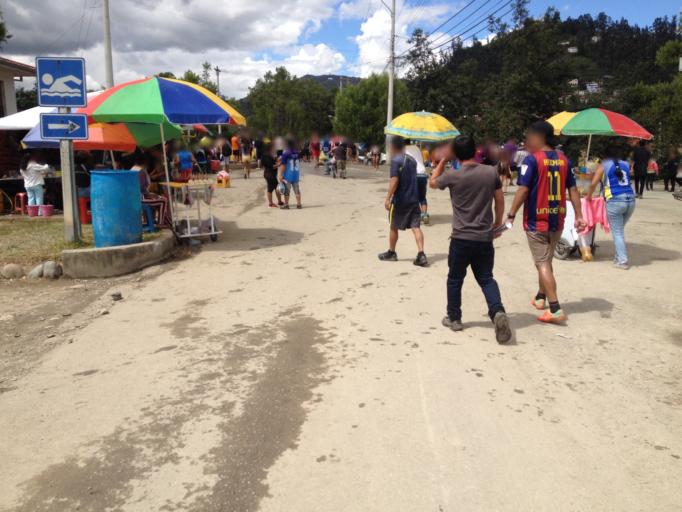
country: EC
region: Azuay
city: Gualaceo
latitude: -2.8957
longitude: -78.7752
